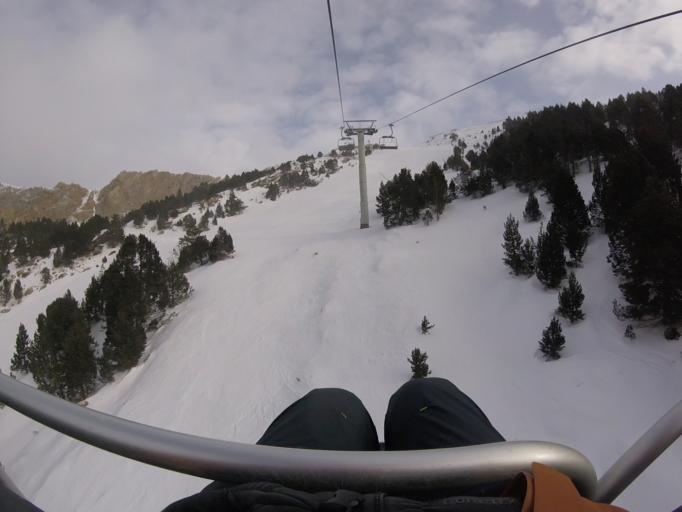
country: AD
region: Canillo
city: Canillo
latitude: 42.5530
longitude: 1.6223
